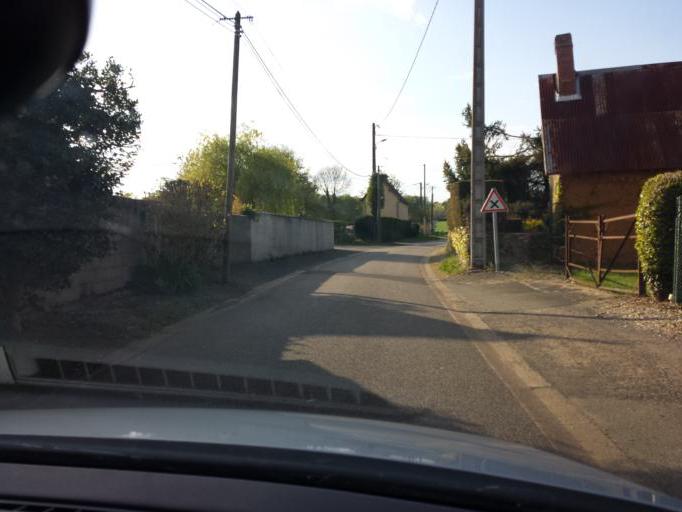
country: FR
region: Haute-Normandie
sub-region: Departement de l'Eure
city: Breteuil
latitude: 48.8094
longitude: 0.9356
